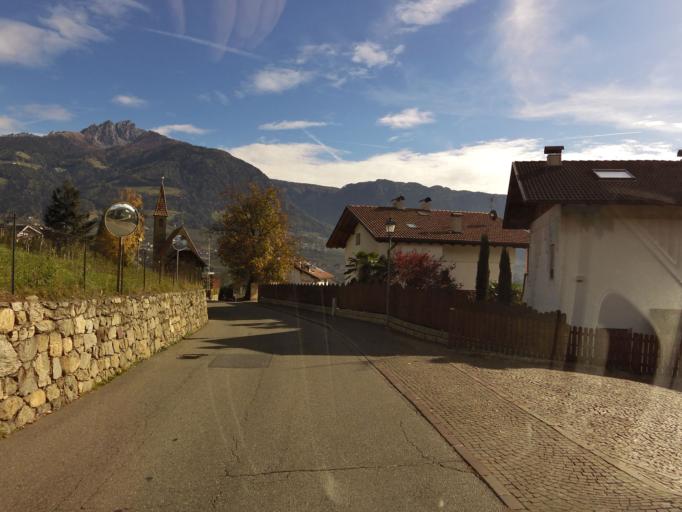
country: IT
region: Trentino-Alto Adige
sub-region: Bolzano
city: Tirolo
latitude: 46.6885
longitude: 11.1586
